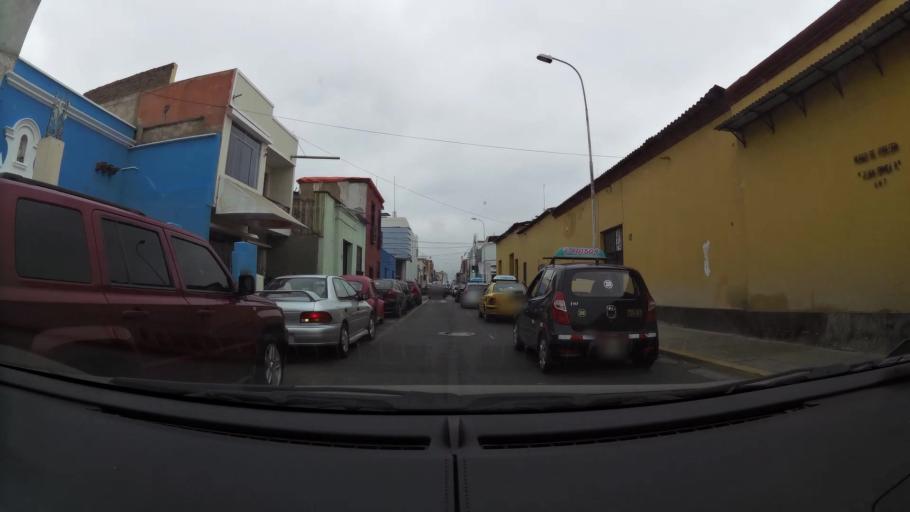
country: PE
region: La Libertad
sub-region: Provincia de Trujillo
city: Trujillo
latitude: -8.1113
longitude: -79.0307
